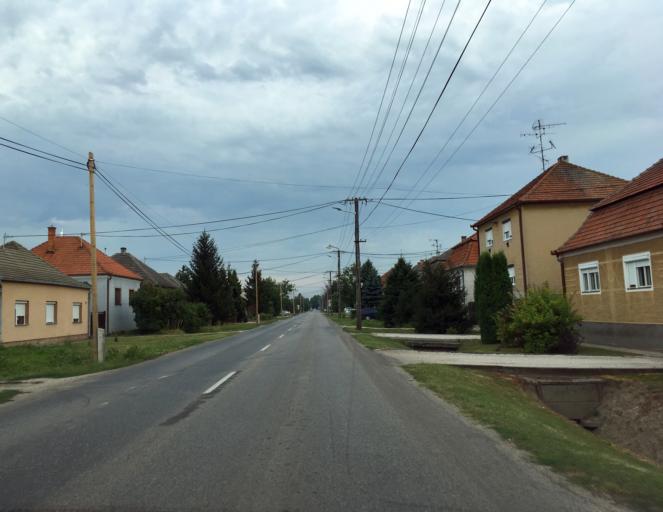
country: SK
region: Nitriansky
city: Kolarovo
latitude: 47.9086
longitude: 18.0058
